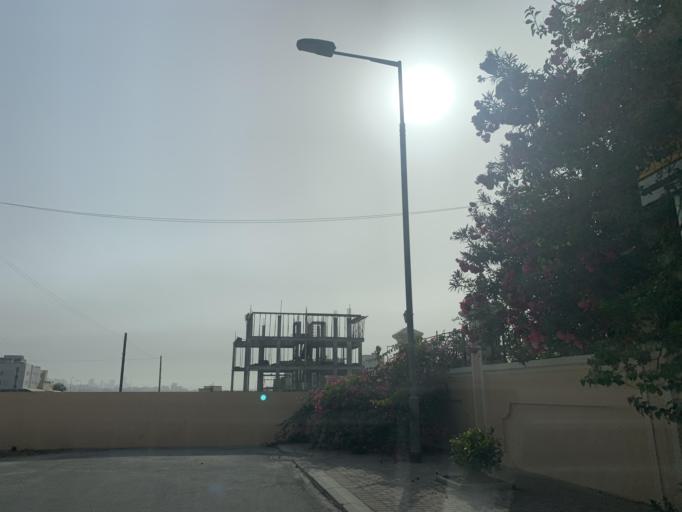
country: BH
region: Northern
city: Madinat `Isa
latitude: 26.1901
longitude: 50.5630
